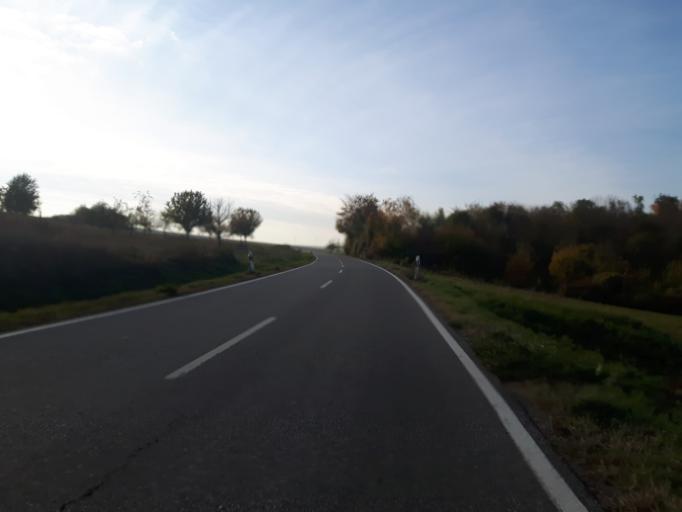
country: DE
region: Rheinland-Pfalz
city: Dintesheim
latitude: 49.7363
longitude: 8.1444
